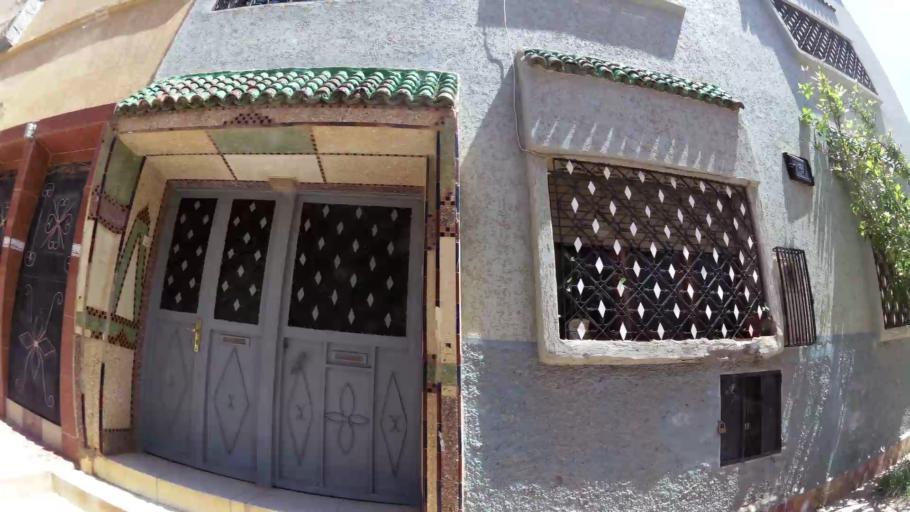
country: MA
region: Rabat-Sale-Zemmour-Zaer
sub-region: Khemisset
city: Khemisset
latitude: 33.8104
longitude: -6.0709
